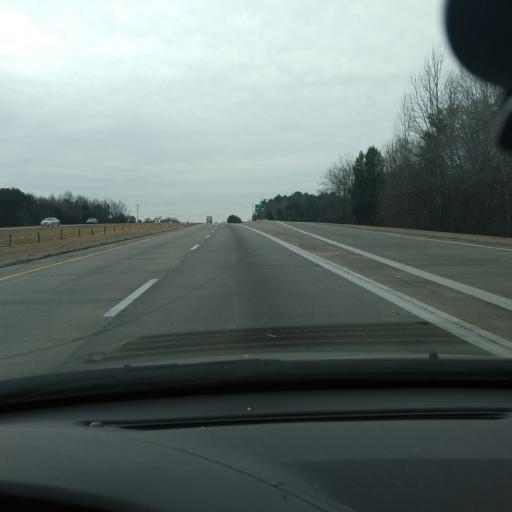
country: US
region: North Carolina
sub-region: Davidson County
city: Midway
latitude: 35.9422
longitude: -80.2353
